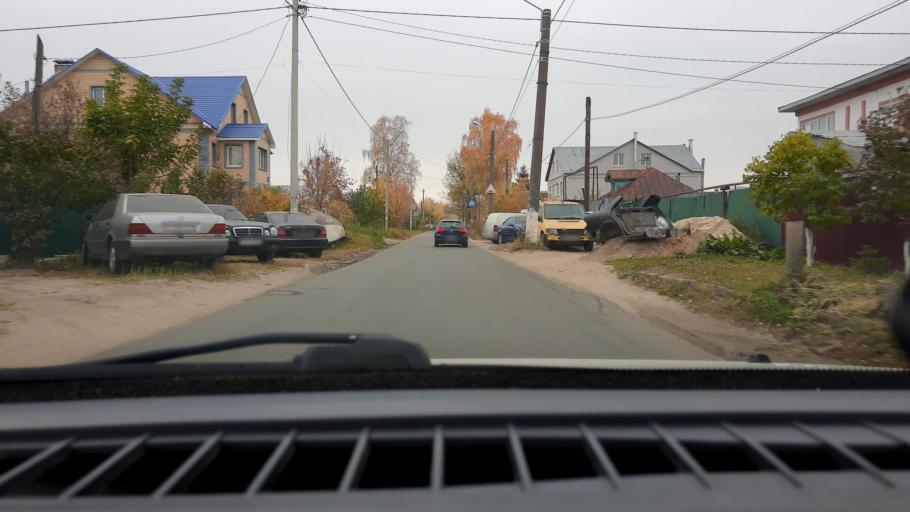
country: RU
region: Nizjnij Novgorod
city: Gorbatovka
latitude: 56.3340
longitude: 43.8307
